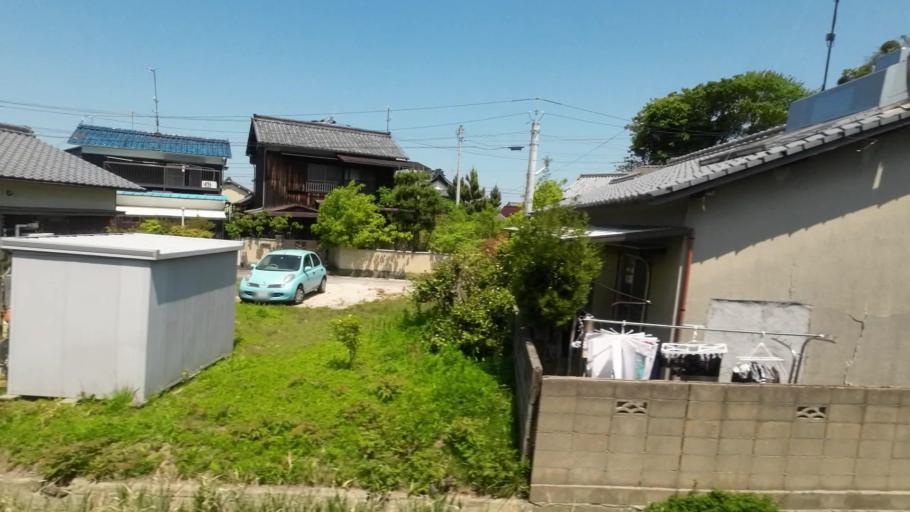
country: JP
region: Ehime
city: Hojo
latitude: 34.0076
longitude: 132.8001
